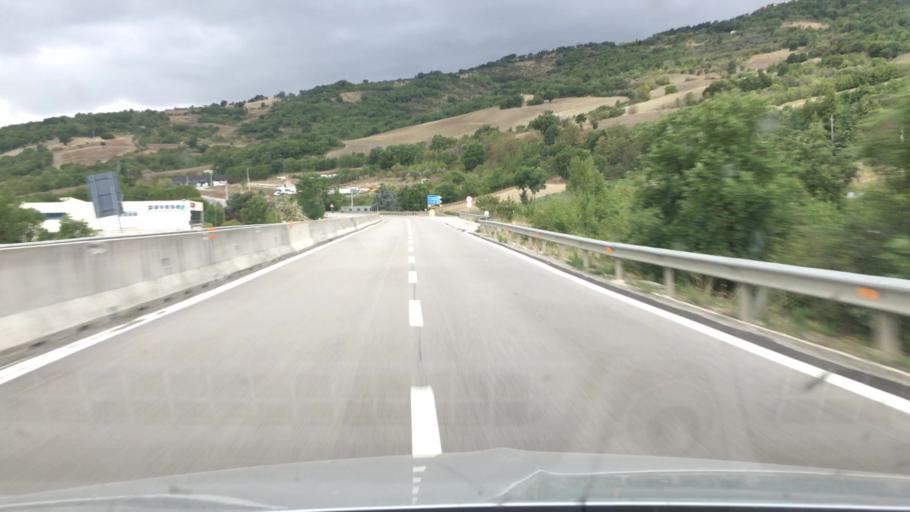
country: IT
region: Basilicate
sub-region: Provincia di Potenza
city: Vaglio Basilicata
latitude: 40.6505
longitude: 15.9291
